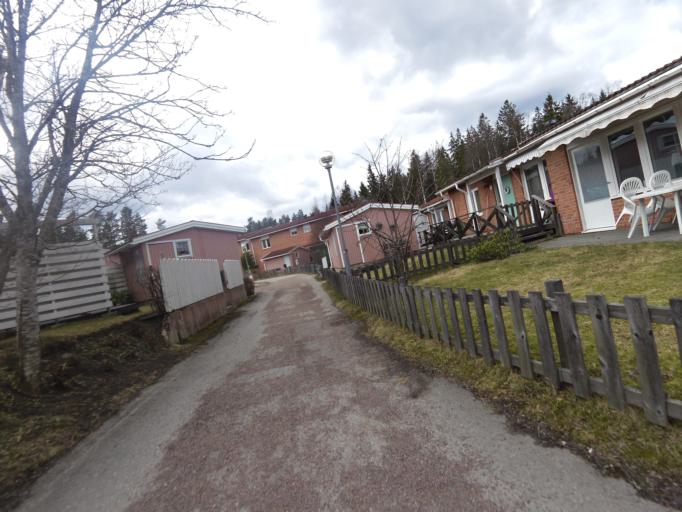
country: SE
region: Gaevleborg
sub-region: Gavle Kommun
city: Gavle
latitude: 60.6905
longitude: 17.0910
